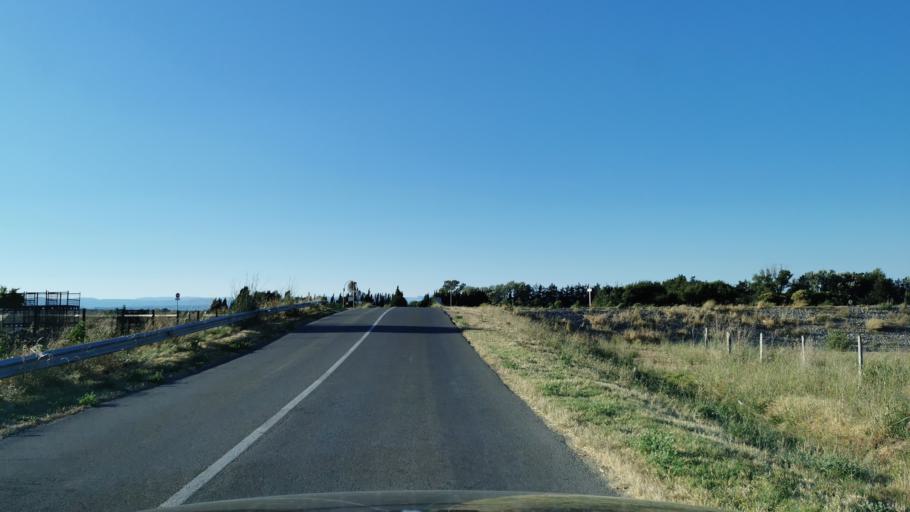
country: FR
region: Languedoc-Roussillon
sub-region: Departement de l'Aude
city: Ouveillan
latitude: 43.2534
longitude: 2.9966
